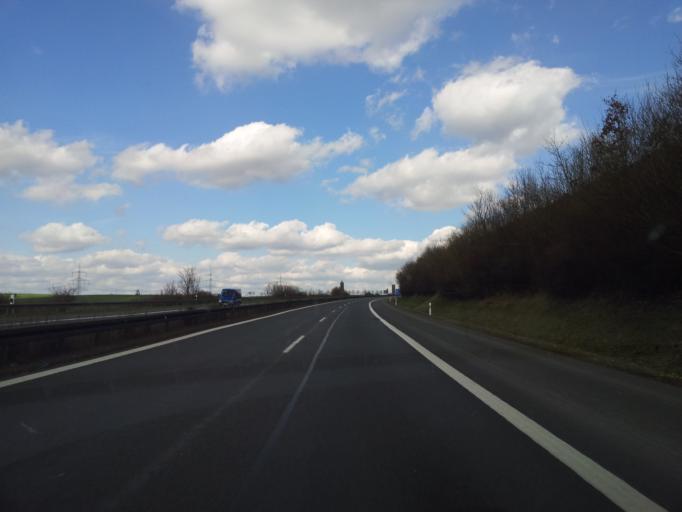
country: DE
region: Bavaria
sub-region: Upper Franconia
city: Memmelsdorf
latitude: 49.9480
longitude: 10.9688
